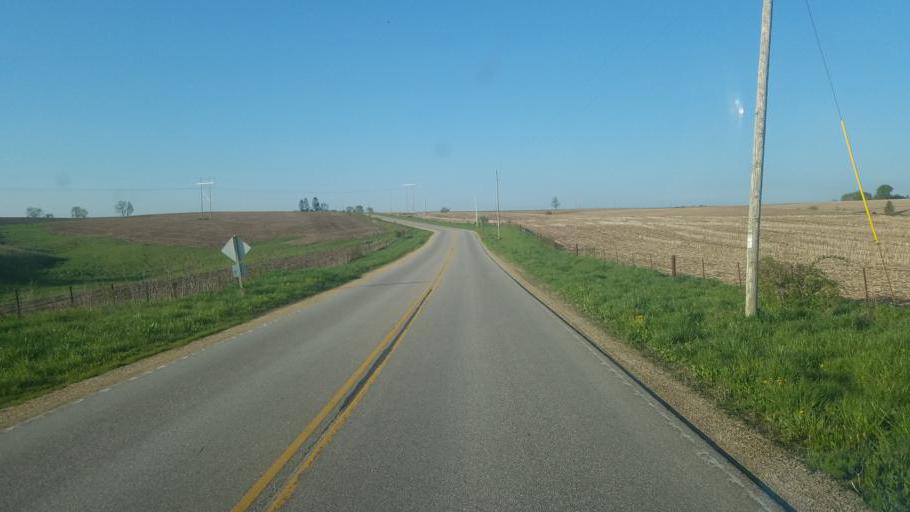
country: US
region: Wisconsin
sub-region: Vernon County
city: Hillsboro
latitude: 43.5743
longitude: -90.5149
